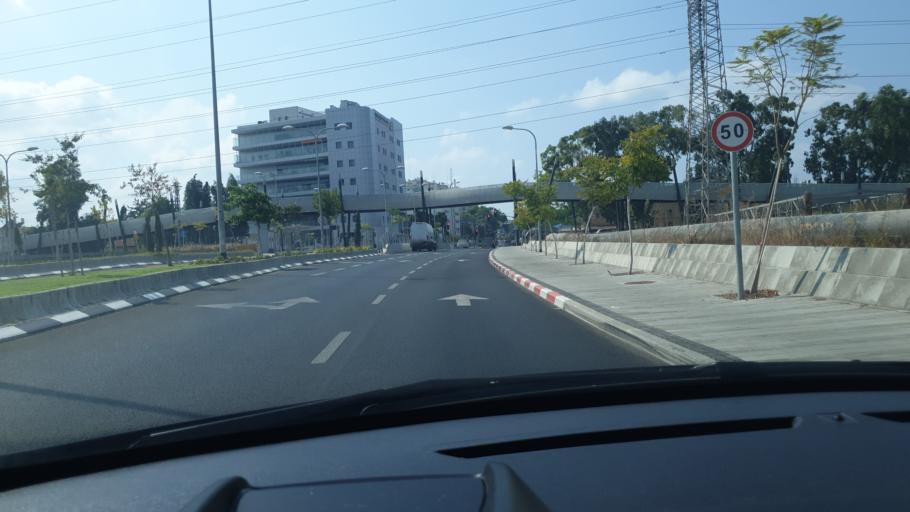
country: IL
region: Haifa
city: Qiryat Bialik
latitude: 32.8157
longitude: 35.0814
